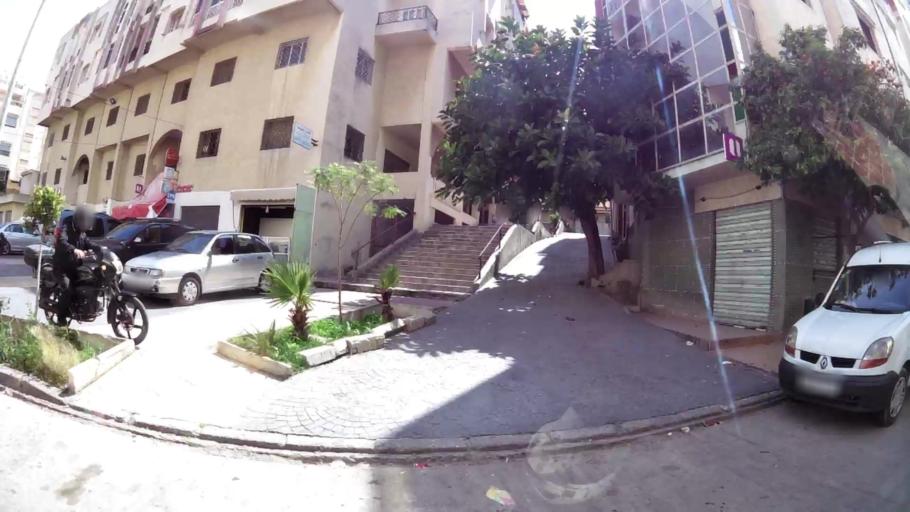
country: MA
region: Tanger-Tetouan
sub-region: Tanger-Assilah
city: Tangier
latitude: 35.7561
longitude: -5.8167
